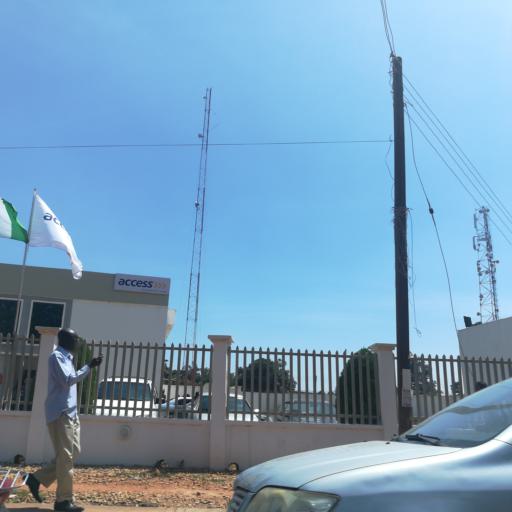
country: NG
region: Plateau
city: Bukuru
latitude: 9.8001
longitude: 8.8680
